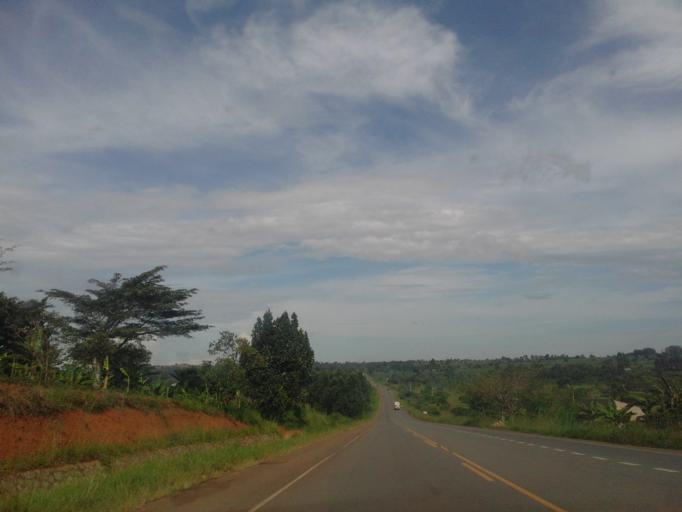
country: UG
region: Central Region
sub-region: Lwengo District
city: Lwengo
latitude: -0.3729
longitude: 31.5219
